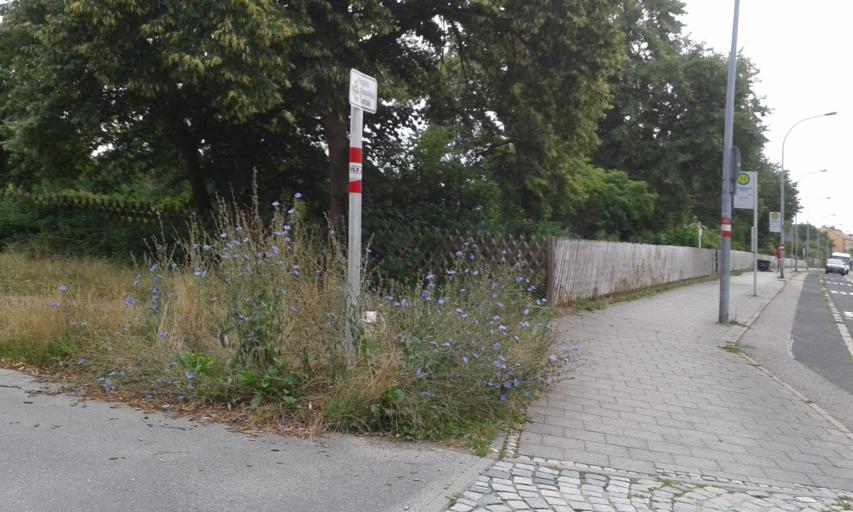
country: DE
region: Bavaria
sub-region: Upper Franconia
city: Bamberg
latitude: 49.8975
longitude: 10.9127
